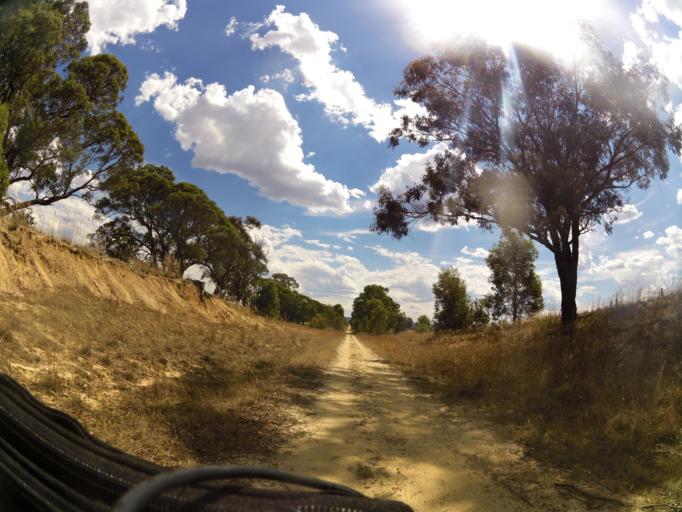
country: AU
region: Victoria
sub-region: Wellington
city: Heyfield
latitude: -37.9793
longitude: 146.7455
